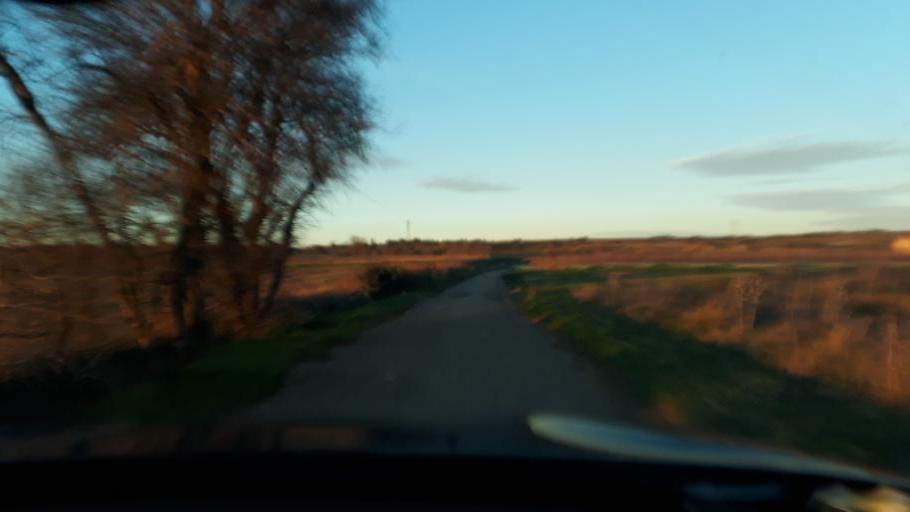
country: FR
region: Languedoc-Roussillon
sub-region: Departement de l'Herault
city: Florensac
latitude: 43.4042
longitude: 3.4599
